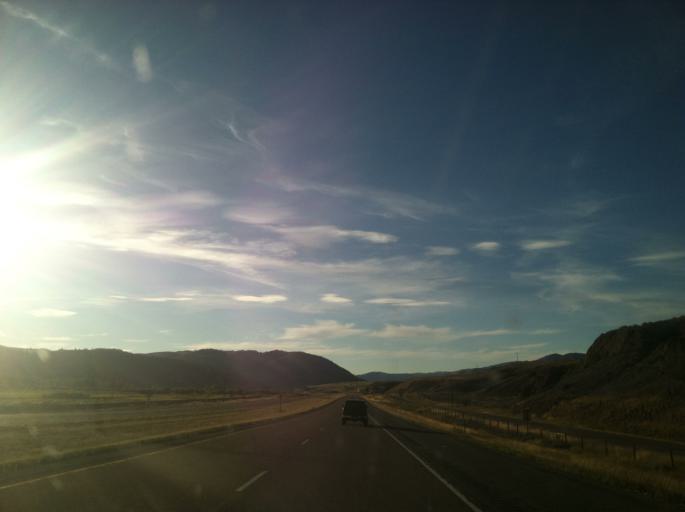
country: US
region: Montana
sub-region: Granite County
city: Philipsburg
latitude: 46.6732
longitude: -113.1620
